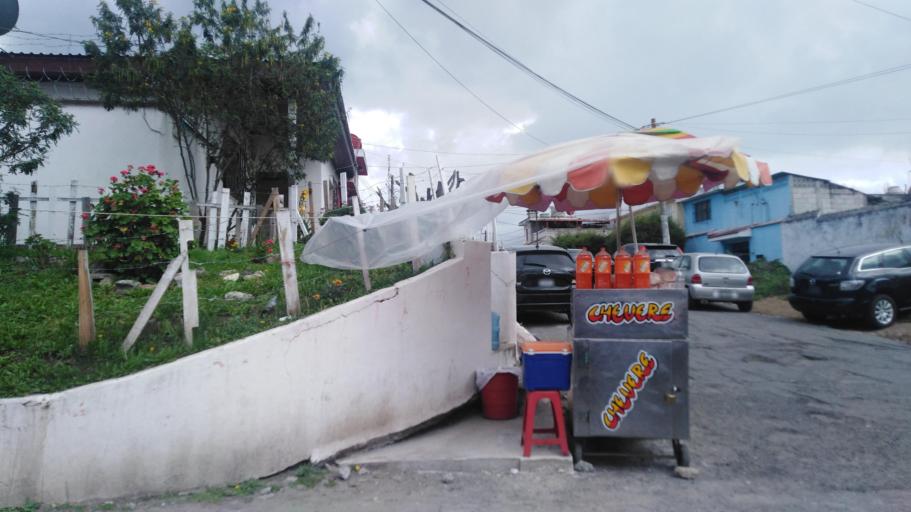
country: GT
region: Quetzaltenango
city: Quetzaltenango
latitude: 14.8452
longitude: -91.5137
